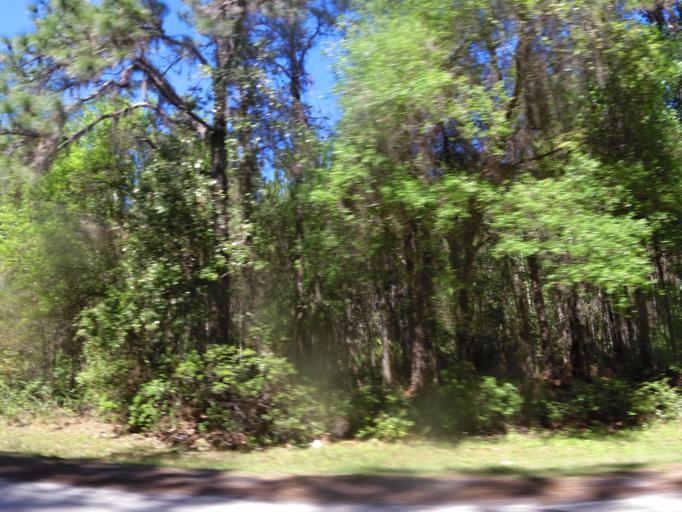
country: US
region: Florida
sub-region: Bradford County
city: Starke
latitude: 30.0559
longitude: -82.0519
